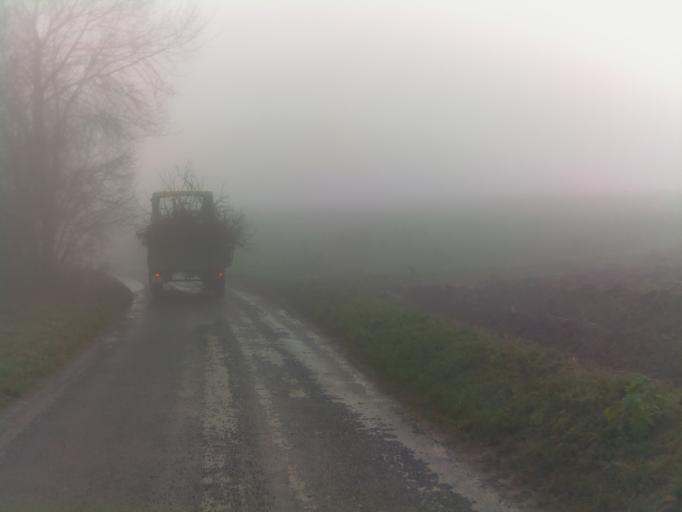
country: DE
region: Bavaria
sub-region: Regierungsbezirk Unterfranken
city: Kreuzwertheim
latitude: 49.7428
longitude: 9.5558
